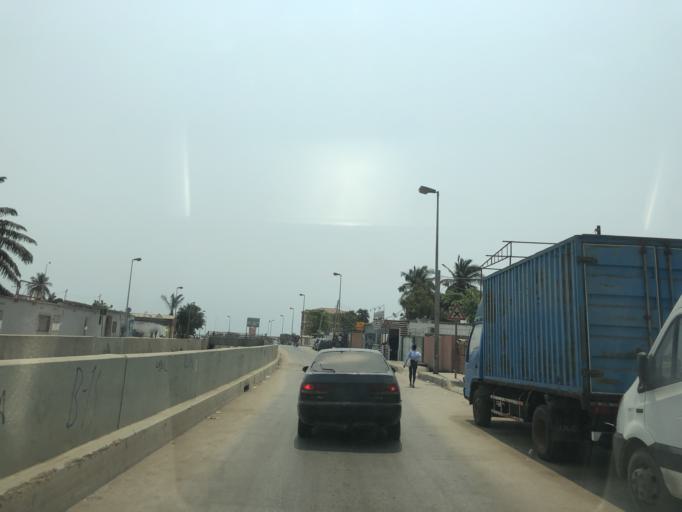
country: AO
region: Luanda
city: Luanda
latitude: -8.8487
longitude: 13.2077
